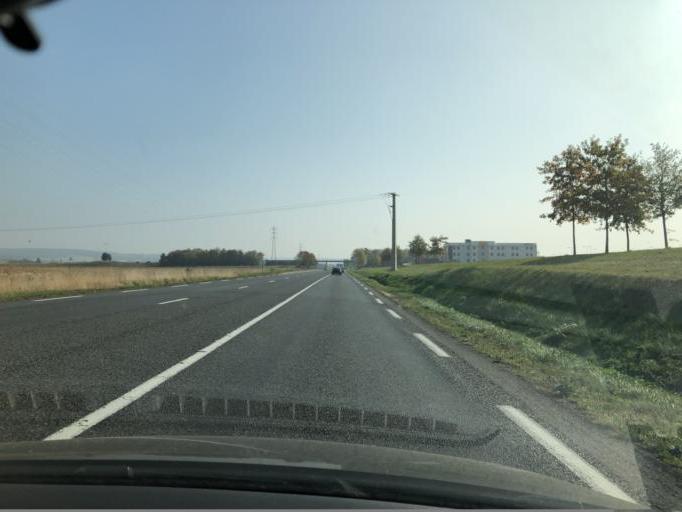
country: FR
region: Bourgogne
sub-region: Departement de l'Yonne
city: Saint-Clement
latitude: 48.2258
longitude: 3.2829
